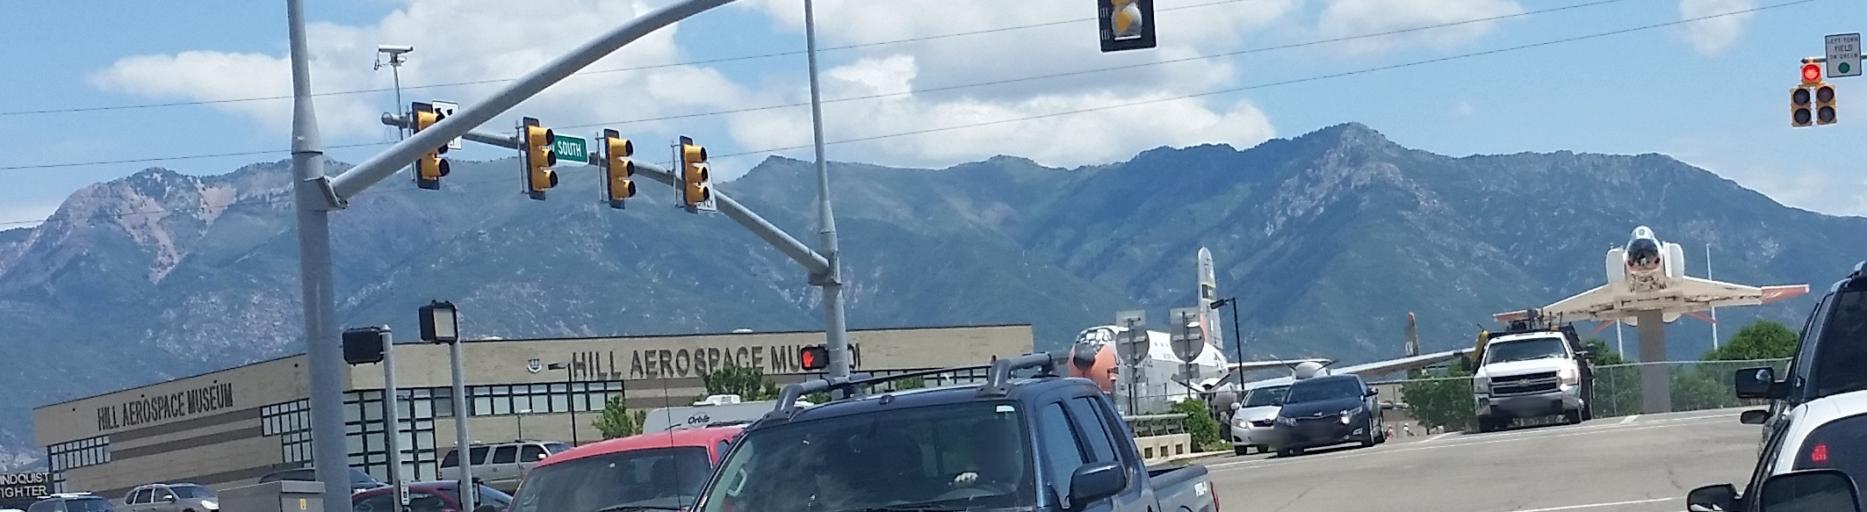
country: US
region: Utah
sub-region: Weber County
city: Roy
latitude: 41.1617
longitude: -112.0226
